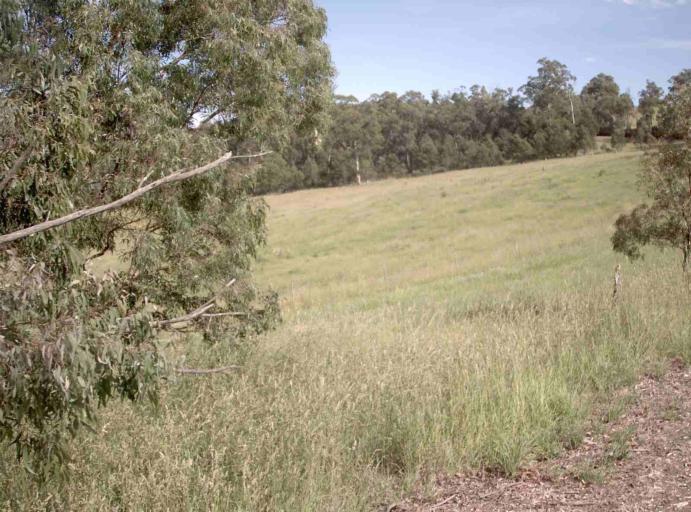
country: AU
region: Victoria
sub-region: East Gippsland
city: Lakes Entrance
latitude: -37.4899
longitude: 148.1305
